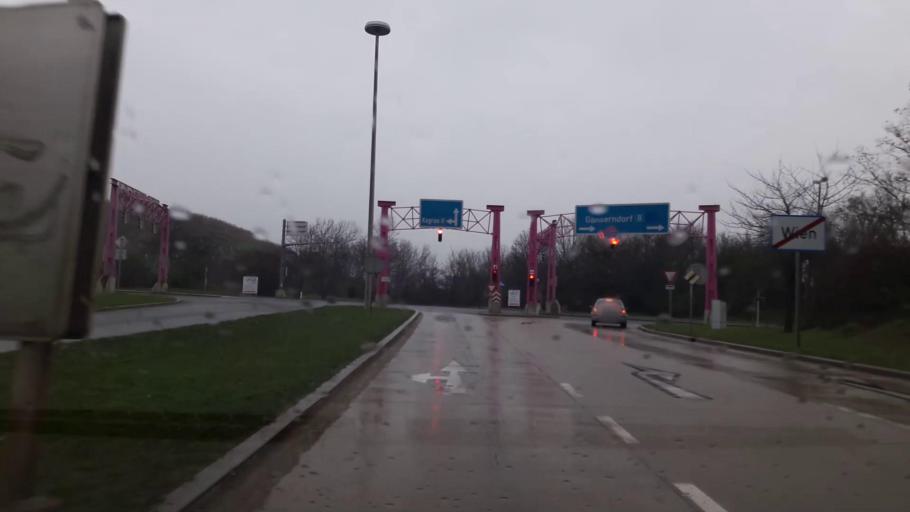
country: AT
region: Lower Austria
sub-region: Politischer Bezirk Wien-Umgebung
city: Gerasdorf bei Wien
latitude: 48.2743
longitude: 16.4734
